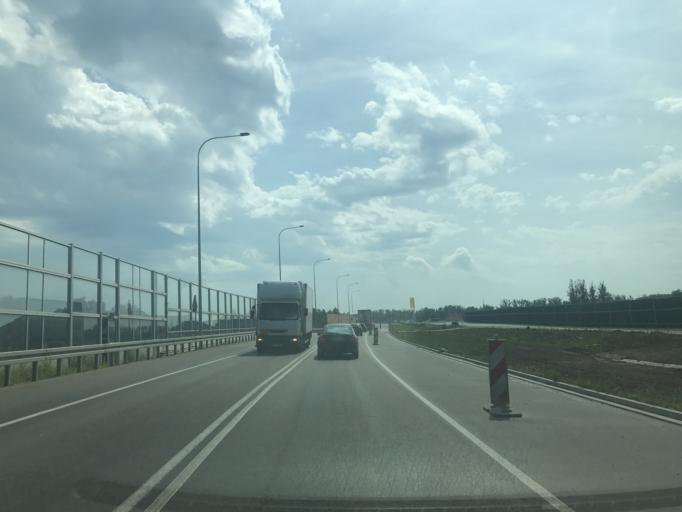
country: PL
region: Warmian-Masurian Voivodeship
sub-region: Powiat ostrodzki
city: Ostroda
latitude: 53.7067
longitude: 19.9781
